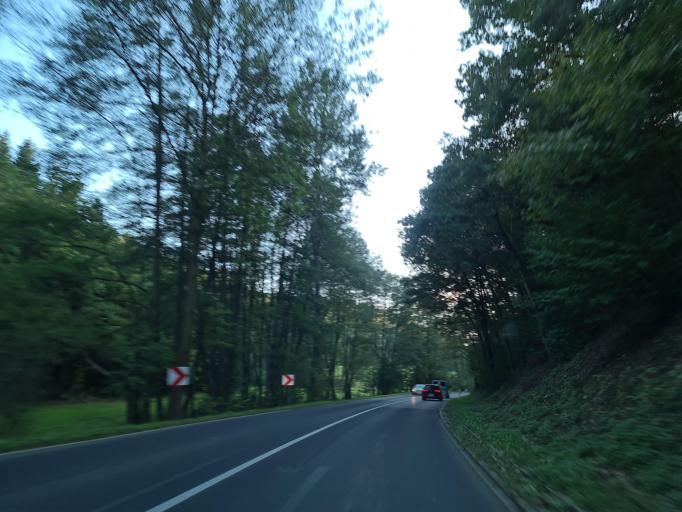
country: DE
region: Saxony
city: Elsterberg
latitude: 50.6036
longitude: 12.1459
